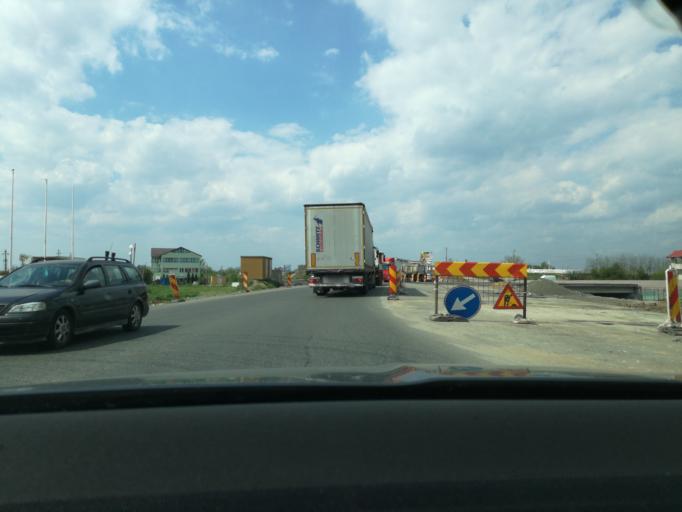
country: RO
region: Ilfov
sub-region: Comuna Chiajna
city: Chiajna
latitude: 44.4533
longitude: 25.9608
